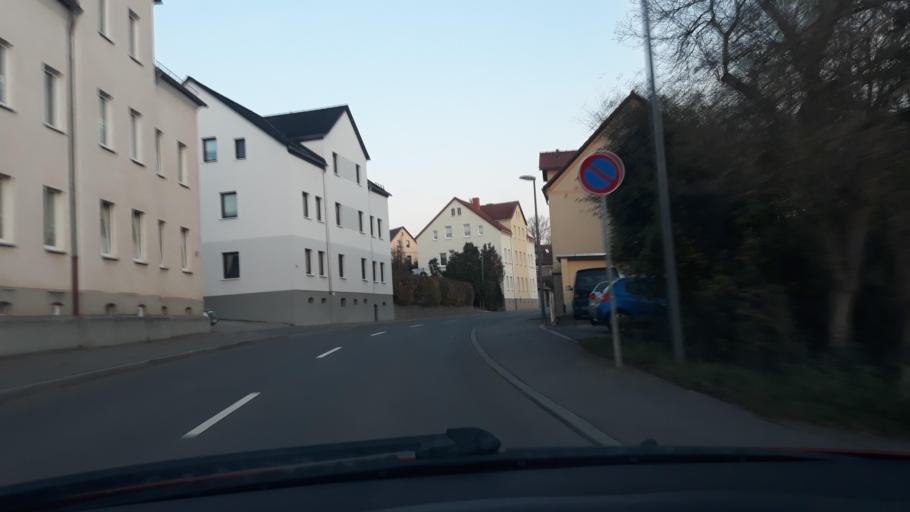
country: DE
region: Saxony
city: Reinsdorf
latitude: 50.6844
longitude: 12.5532
